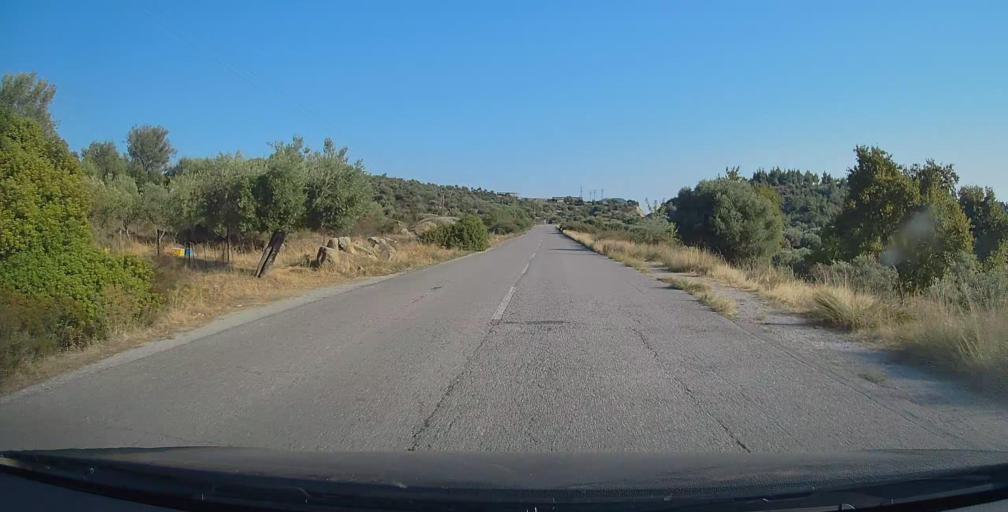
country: GR
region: Central Macedonia
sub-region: Nomos Chalkidikis
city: Sykia
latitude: 40.0038
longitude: 23.8865
